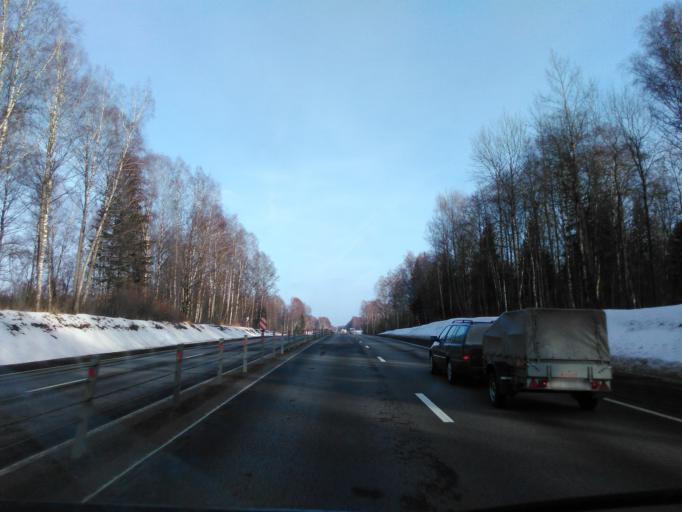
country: RU
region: Smolensk
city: Vyaz'ma
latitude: 55.1889
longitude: 34.0271
